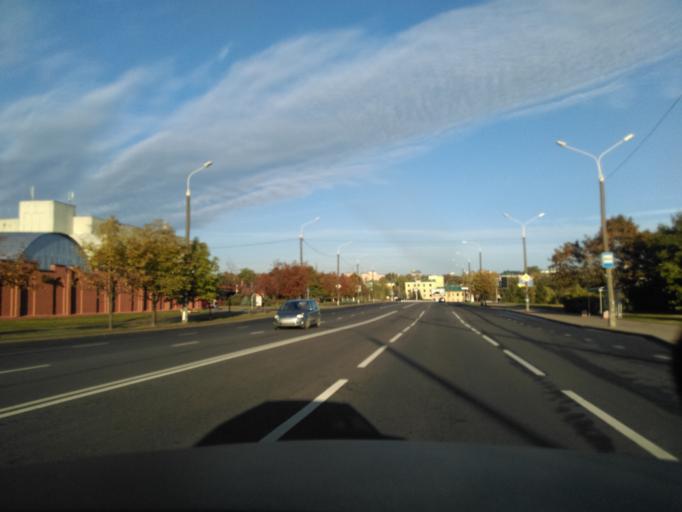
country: BY
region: Minsk
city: Minsk
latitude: 53.8939
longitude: 27.5698
